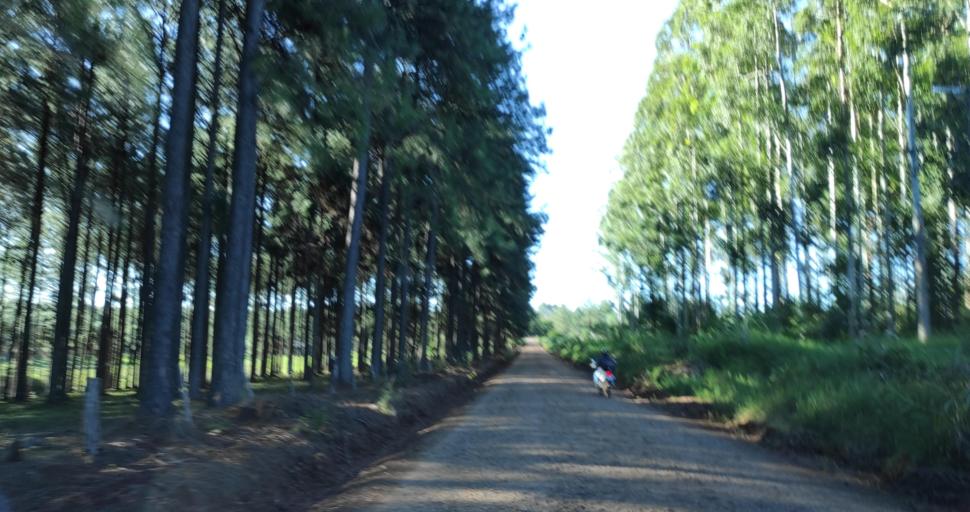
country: AR
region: Misiones
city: Puerto Rico
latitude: -26.8290
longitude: -55.0013
